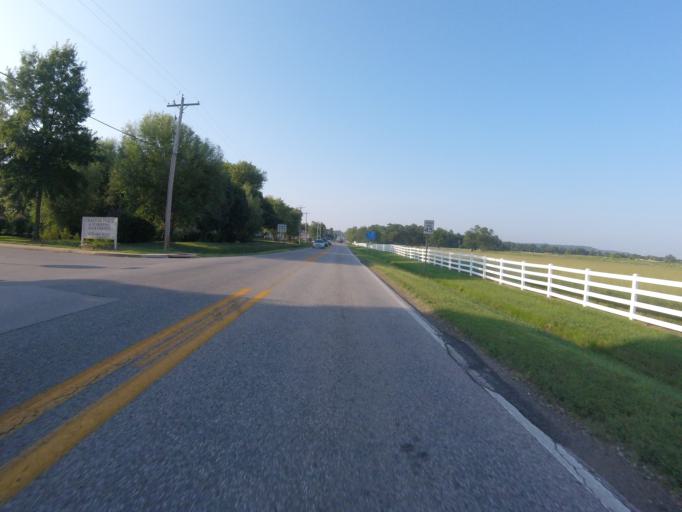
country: US
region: Arkansas
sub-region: Washington County
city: Fayetteville
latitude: 36.0919
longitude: -94.1749
